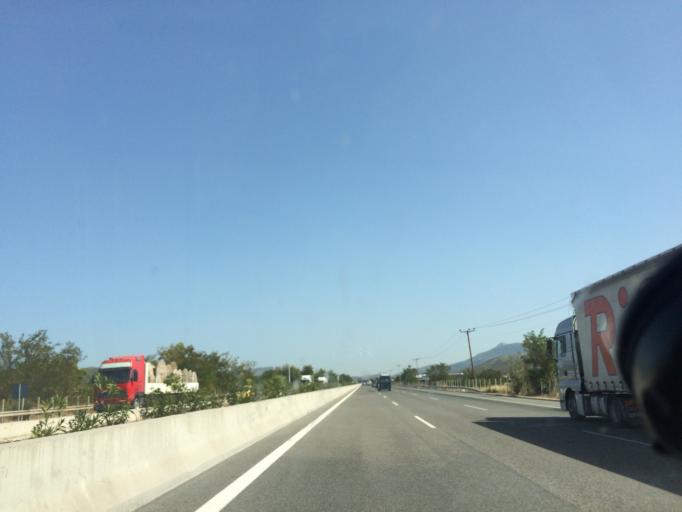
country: GR
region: Attica
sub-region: Nomarchia Anatolikis Attikis
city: Avlonas
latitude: 38.2647
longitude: 23.7181
